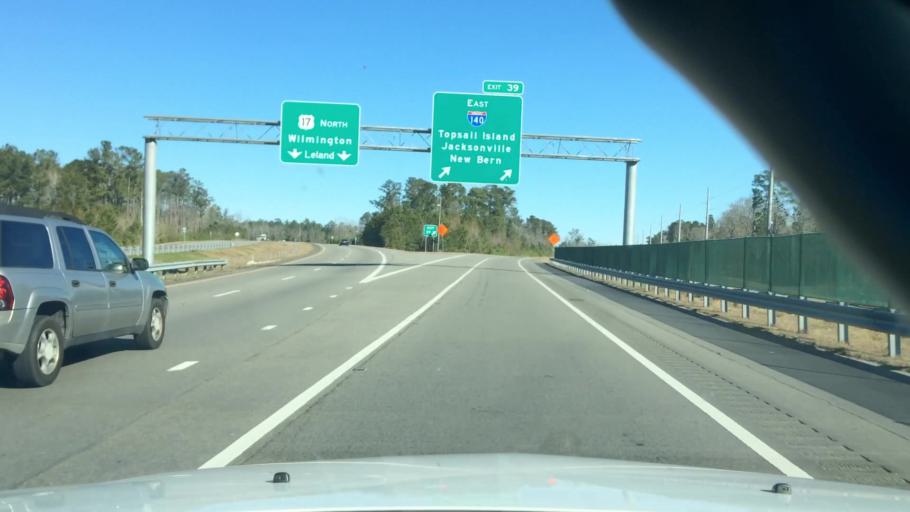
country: US
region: North Carolina
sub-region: Brunswick County
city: Leland
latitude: 34.1823
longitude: -78.0827
